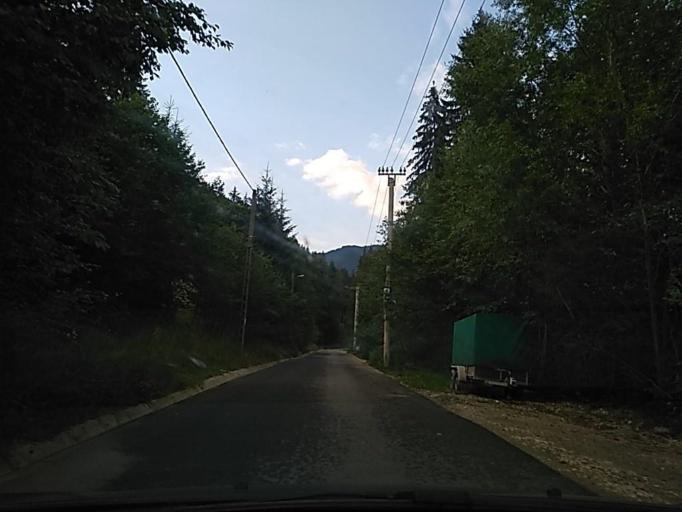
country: RO
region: Brasov
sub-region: Comuna Bran
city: Simon
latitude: 45.4898
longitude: 25.3844
